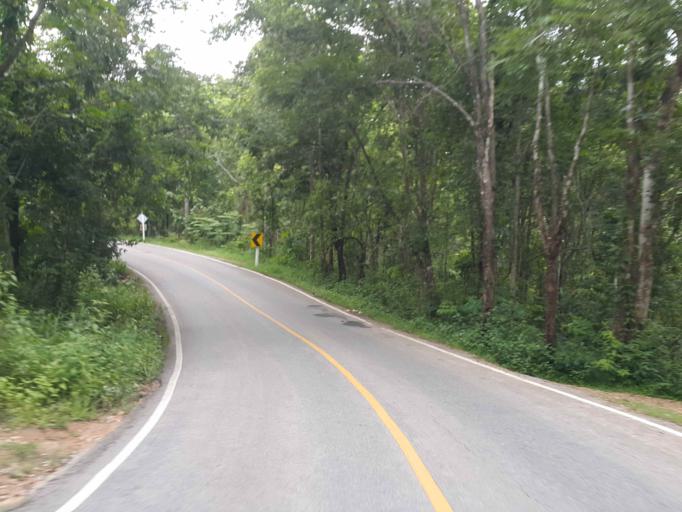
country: TH
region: Chiang Mai
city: Mae Chaem
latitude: 18.5156
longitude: 98.4176
